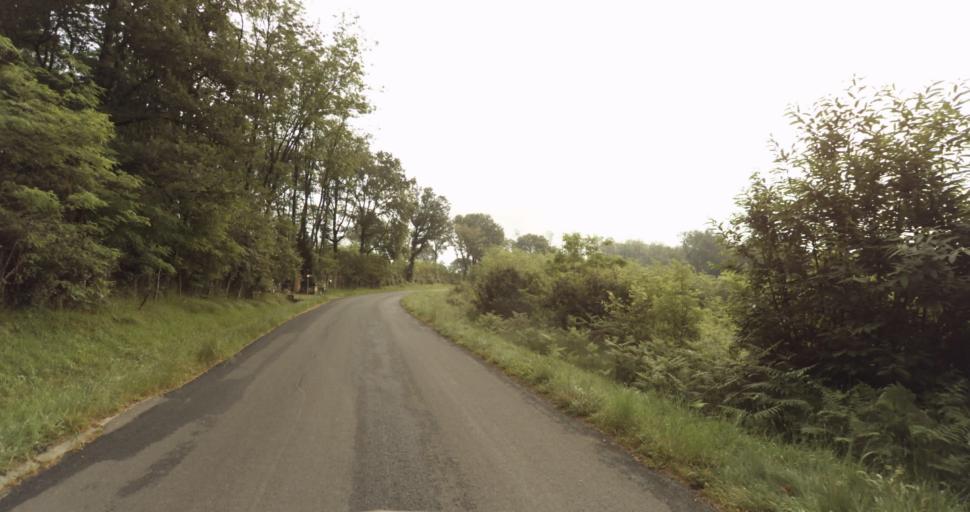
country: FR
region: Aquitaine
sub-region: Departement de la Dordogne
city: Lalinde
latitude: 44.9005
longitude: 0.7715
